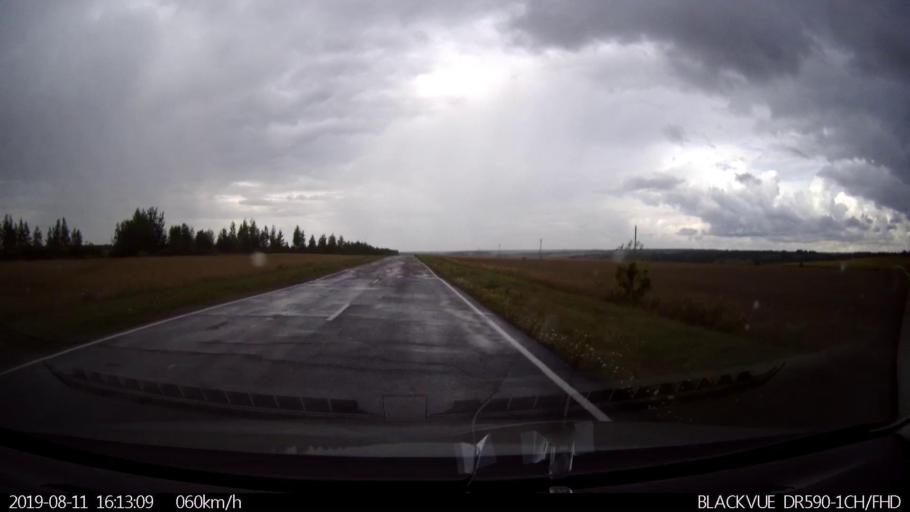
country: RU
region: Ulyanovsk
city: Ignatovka
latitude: 54.0178
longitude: 47.6379
